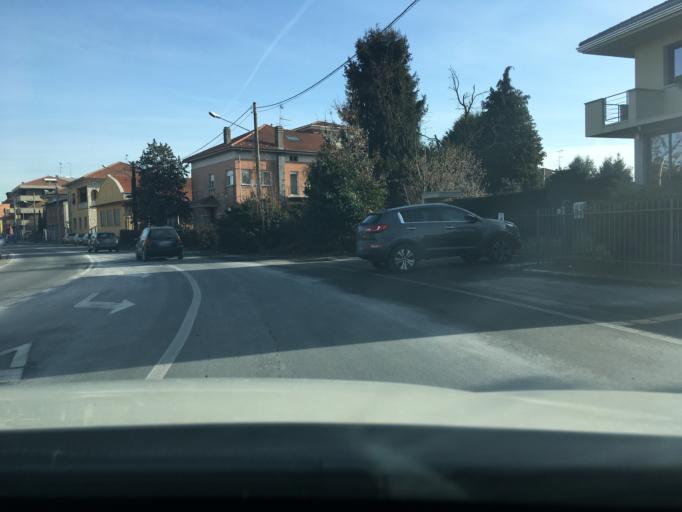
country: IT
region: Piedmont
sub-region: Provincia di Novara
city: Borgomanero
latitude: 45.6917
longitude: 8.4657
